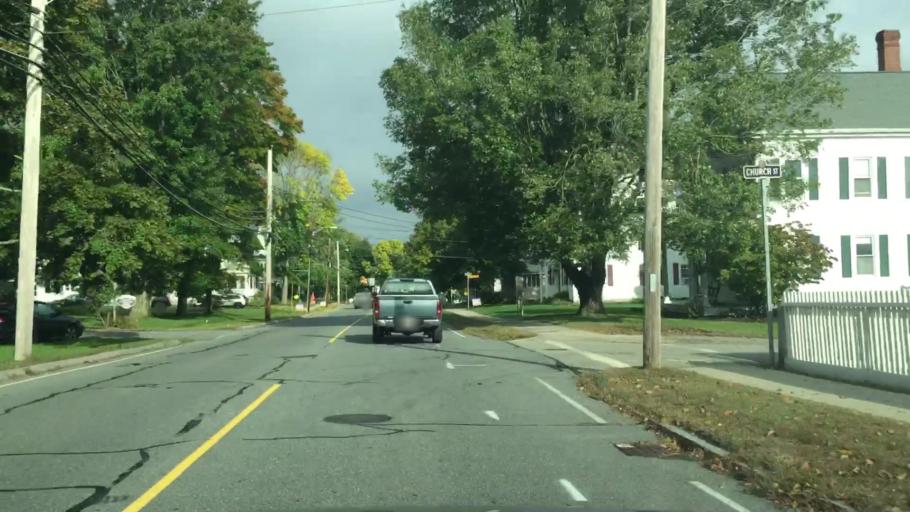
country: US
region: Massachusetts
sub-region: Essex County
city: North Andover
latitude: 42.6986
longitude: -71.1281
